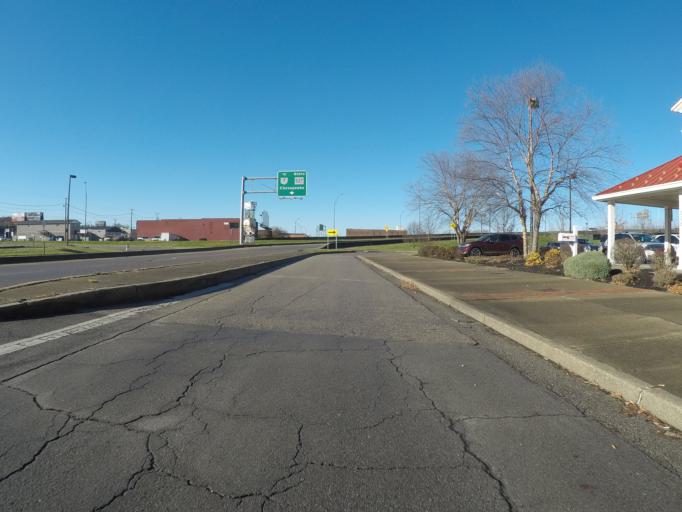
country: US
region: West Virginia
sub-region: Cabell County
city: Huntington
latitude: 38.4212
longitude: -82.4487
